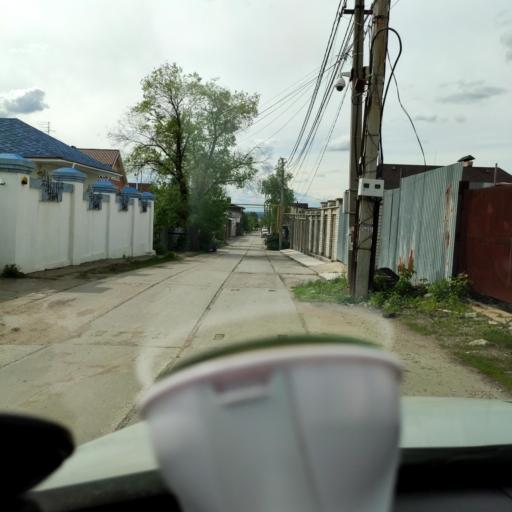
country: RU
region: Samara
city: Samara
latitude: 53.2645
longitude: 50.2061
